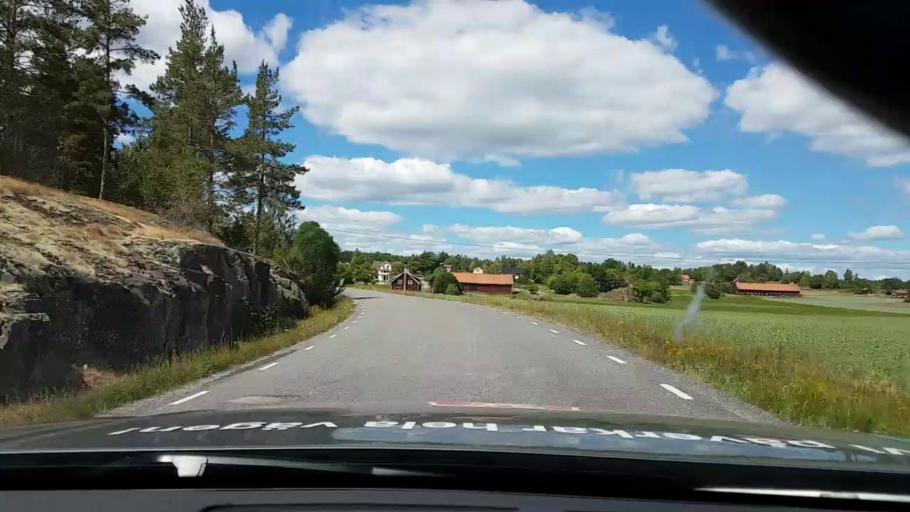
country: SE
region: Kalmar
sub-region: Vasterviks Kommun
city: Forserum
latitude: 58.0059
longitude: 16.5851
